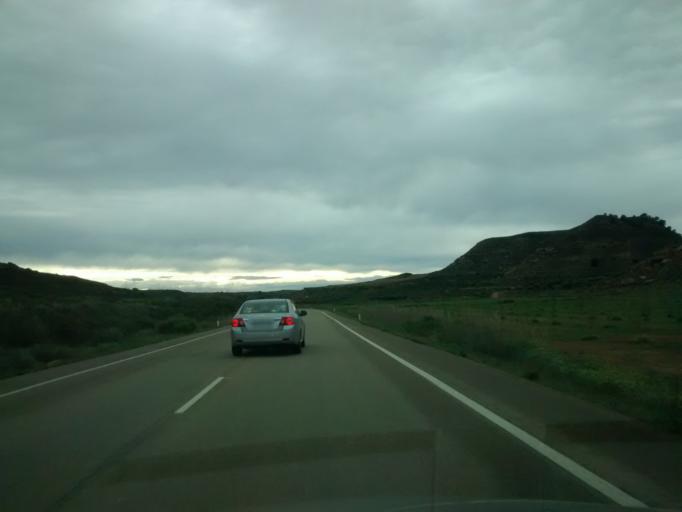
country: ES
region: Aragon
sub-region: Provincia de Zaragoza
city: Caspe
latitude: 41.2085
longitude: 0.0285
